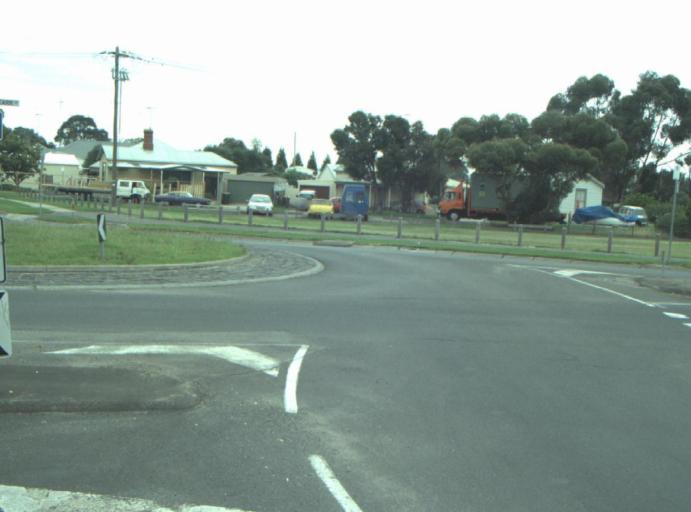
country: AU
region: Victoria
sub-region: Greater Geelong
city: East Geelong
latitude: -38.1677
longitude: 144.3725
